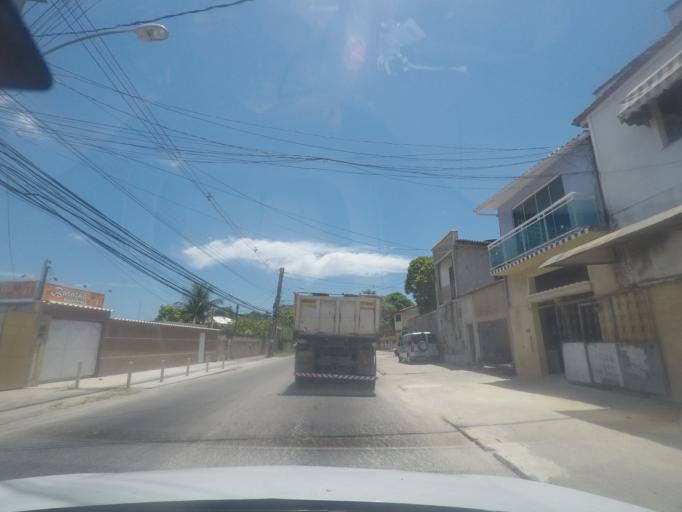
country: BR
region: Rio de Janeiro
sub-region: Itaguai
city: Itaguai
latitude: -22.9314
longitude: -43.6898
